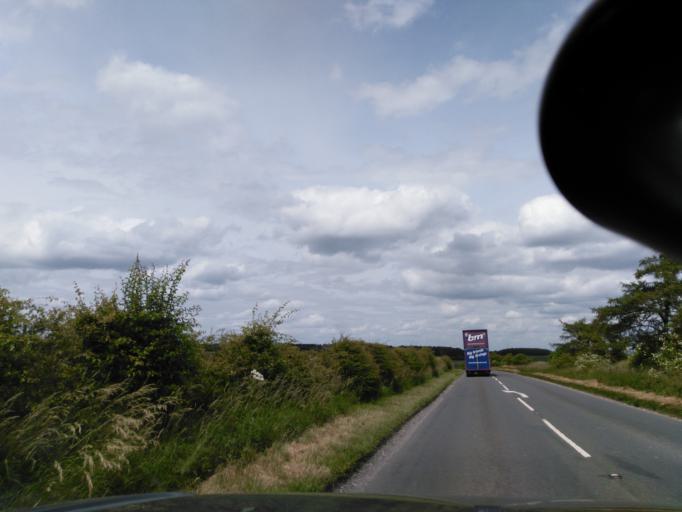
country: GB
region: England
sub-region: Wiltshire
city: Woodford
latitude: 51.1334
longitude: -1.8572
